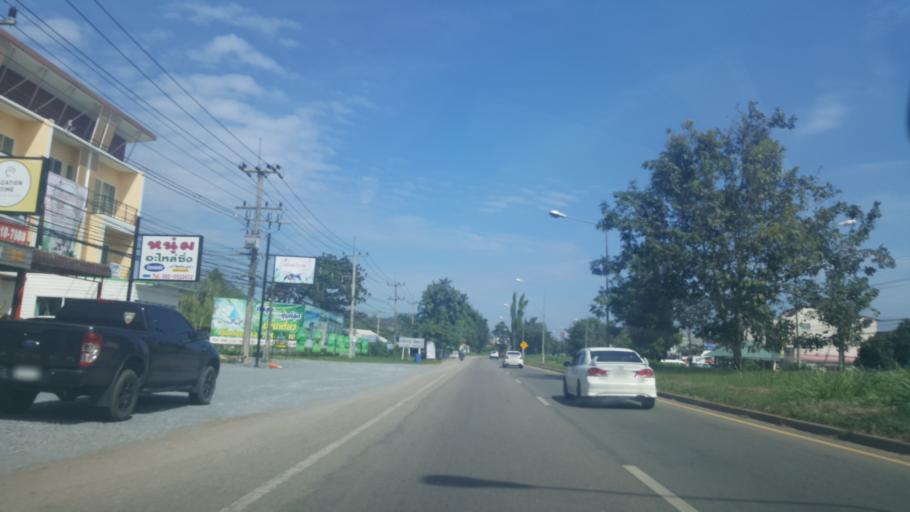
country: TH
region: Chon Buri
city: Sattahip
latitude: 12.7170
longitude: 100.8874
